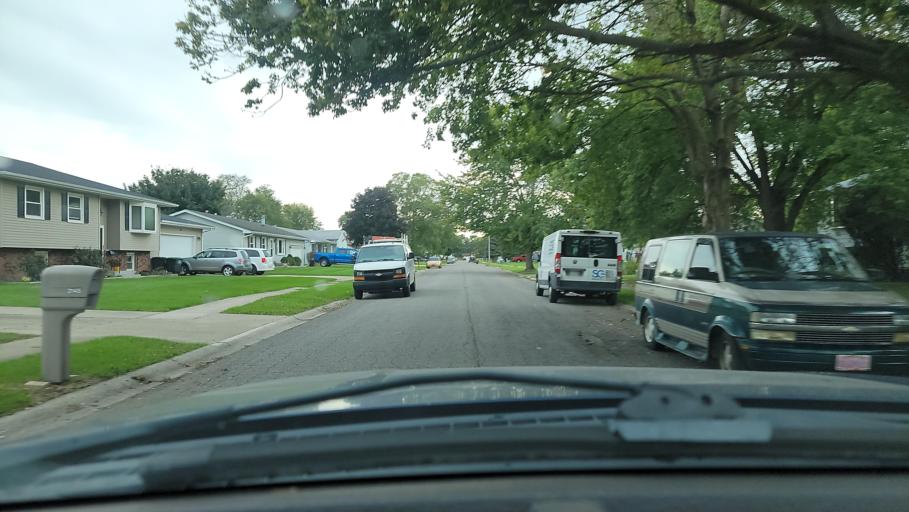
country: US
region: Indiana
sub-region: Lake County
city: Lake Station
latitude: 41.5609
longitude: -87.2126
